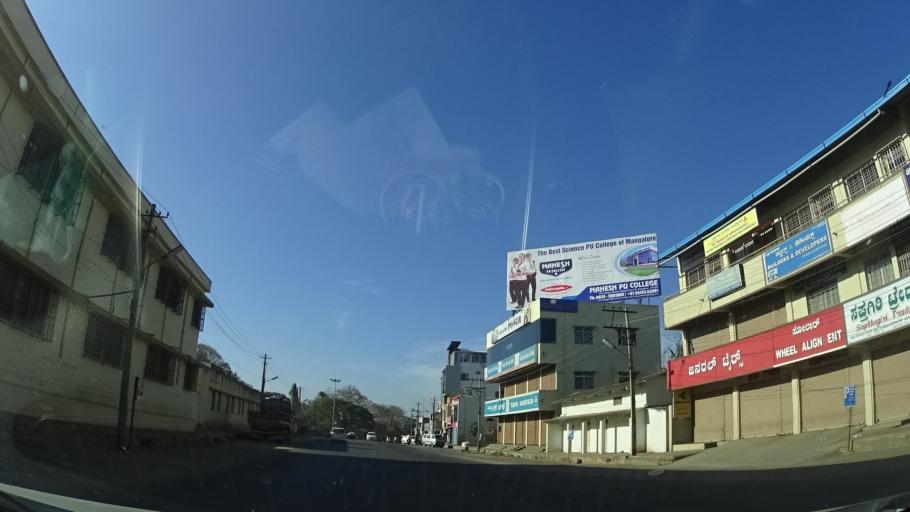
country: IN
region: Karnataka
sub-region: Chikmagalur
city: Chikmagalur
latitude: 13.3149
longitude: 75.7713
